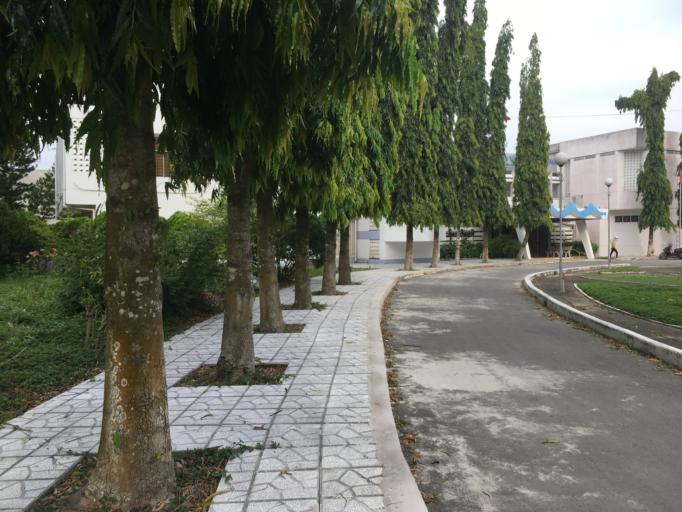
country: VN
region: Can Tho
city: Can Tho
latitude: 10.0308
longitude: 105.7685
